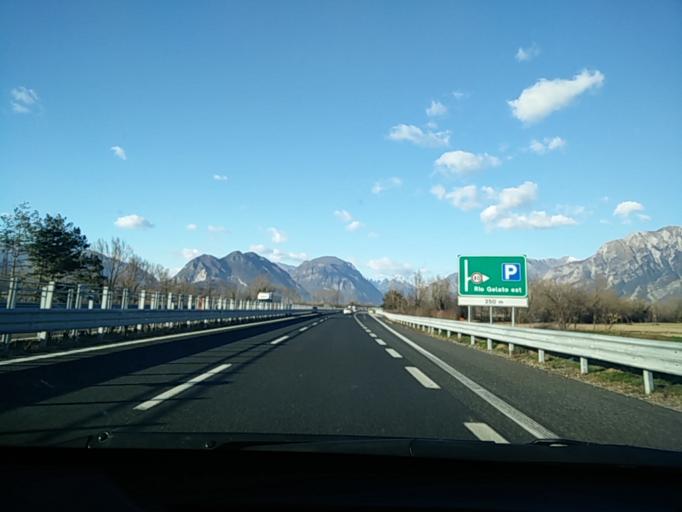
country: IT
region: Friuli Venezia Giulia
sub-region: Provincia di Udine
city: Buia
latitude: 46.2204
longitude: 13.0931
